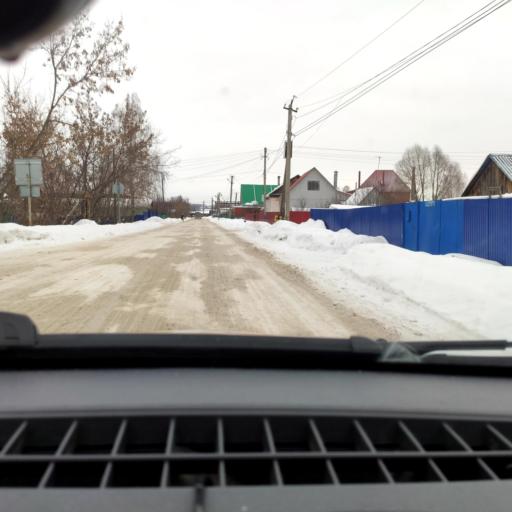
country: RU
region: Bashkortostan
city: Iglino
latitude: 54.8282
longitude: 56.3974
